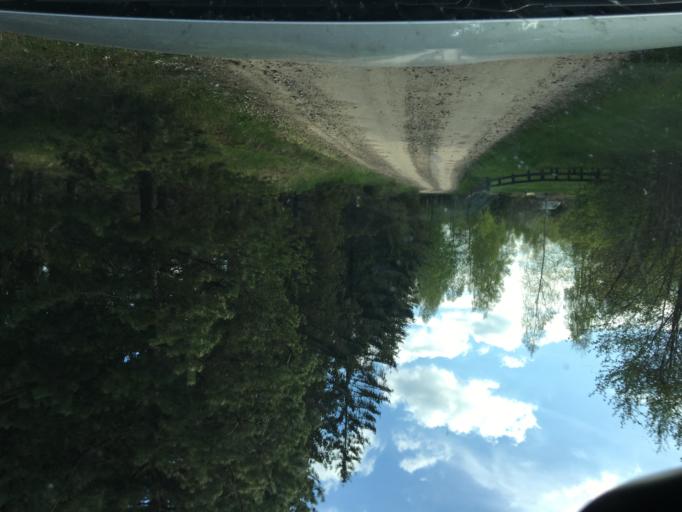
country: LV
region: Ozolnieku
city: Ozolnieki
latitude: 56.6701
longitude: 23.8767
